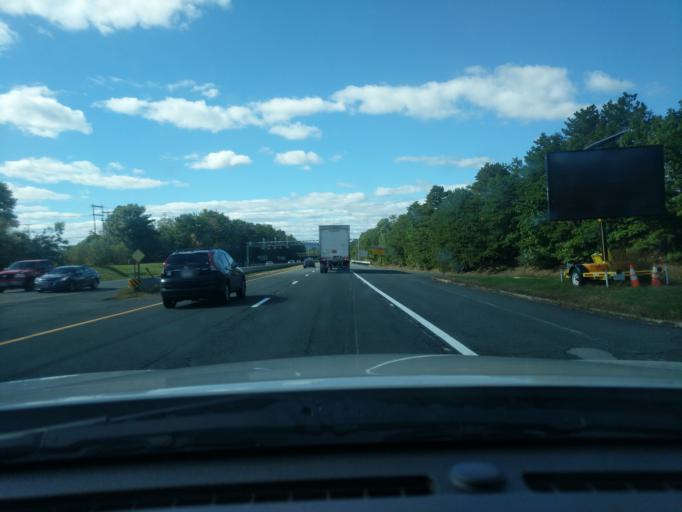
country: US
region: Massachusetts
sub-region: Hampden County
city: Westfield
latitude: 42.1435
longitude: -72.7256
